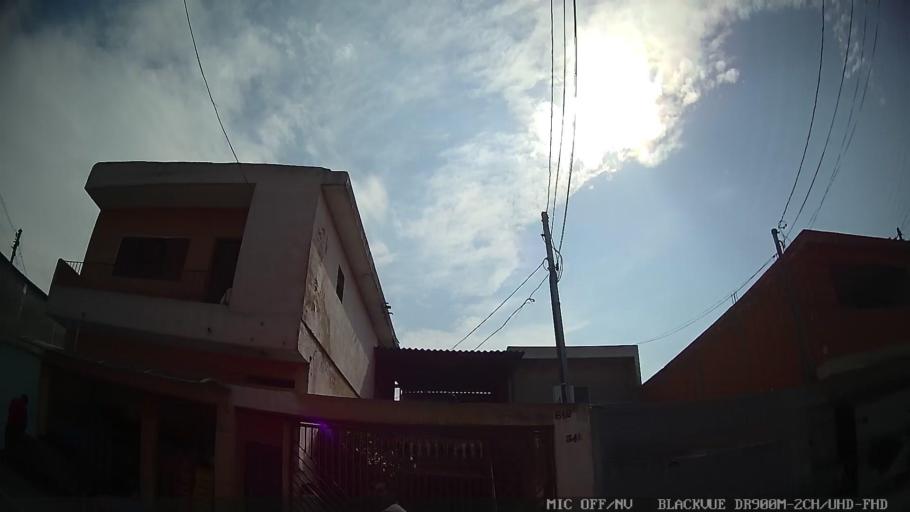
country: BR
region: Sao Paulo
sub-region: Ferraz De Vasconcelos
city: Ferraz de Vasconcelos
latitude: -23.5149
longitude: -46.4147
